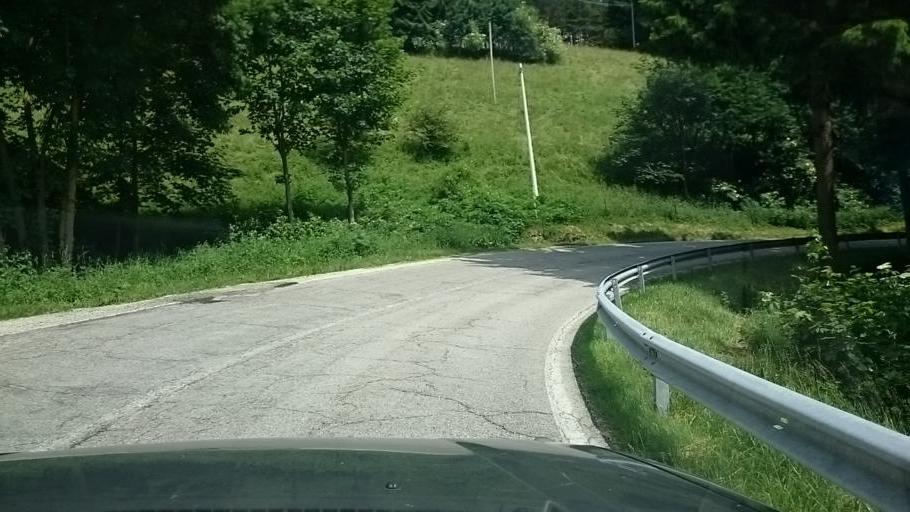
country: IT
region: Veneto
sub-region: Provincia di Vicenza
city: Conco
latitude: 45.8065
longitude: 11.6208
